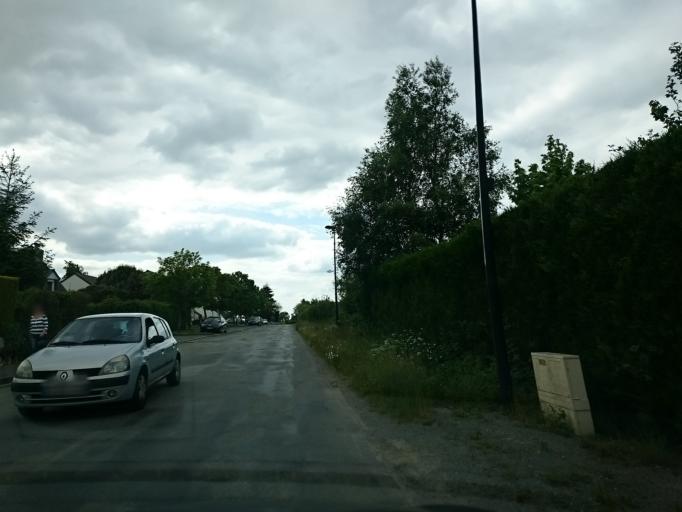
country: FR
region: Brittany
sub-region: Departement d'Ille-et-Vilaine
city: Crevin
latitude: 47.9367
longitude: -1.6560
